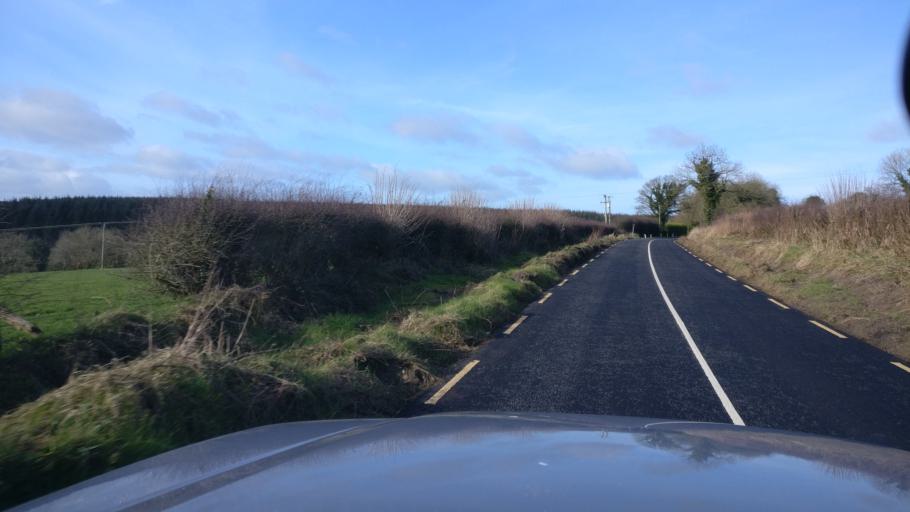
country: IE
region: Leinster
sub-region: Kilkenny
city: Castlecomer
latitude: 52.9056
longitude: -7.1820
